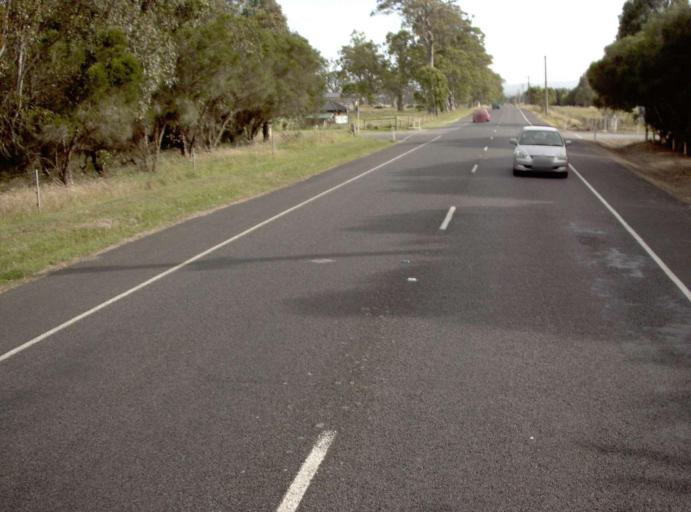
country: AU
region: Victoria
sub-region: Latrobe
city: Traralgon
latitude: -38.1397
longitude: 146.5568
